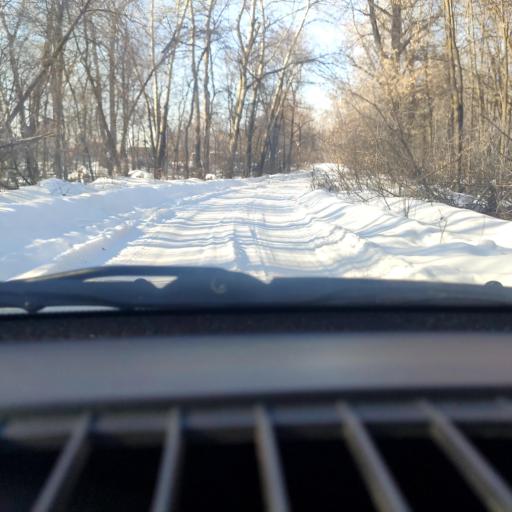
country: RU
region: Bashkortostan
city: Ufa
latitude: 54.6731
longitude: 55.9560
